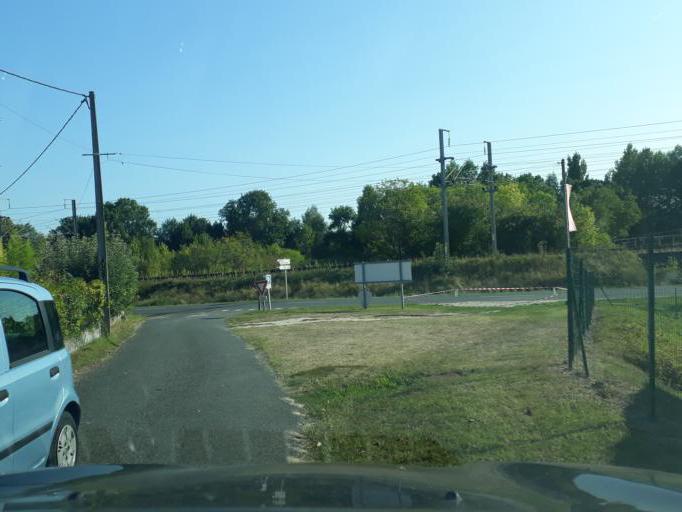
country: FR
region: Centre
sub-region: Departement du Loir-et-Cher
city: Thesee
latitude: 47.3294
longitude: 1.2954
